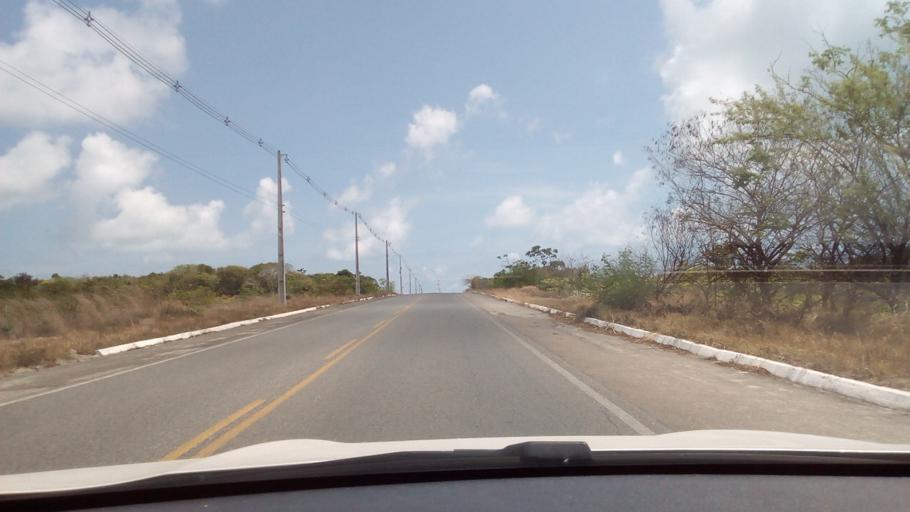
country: BR
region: Paraiba
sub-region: Joao Pessoa
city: Joao Pessoa
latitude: -7.1965
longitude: -34.8073
